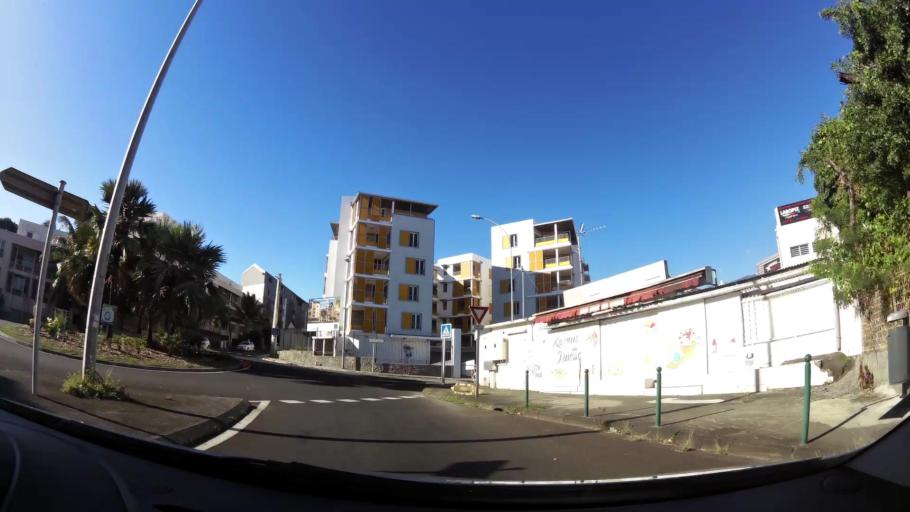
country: RE
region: Reunion
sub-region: Reunion
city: Saint-Denis
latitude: -20.8993
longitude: 55.4752
